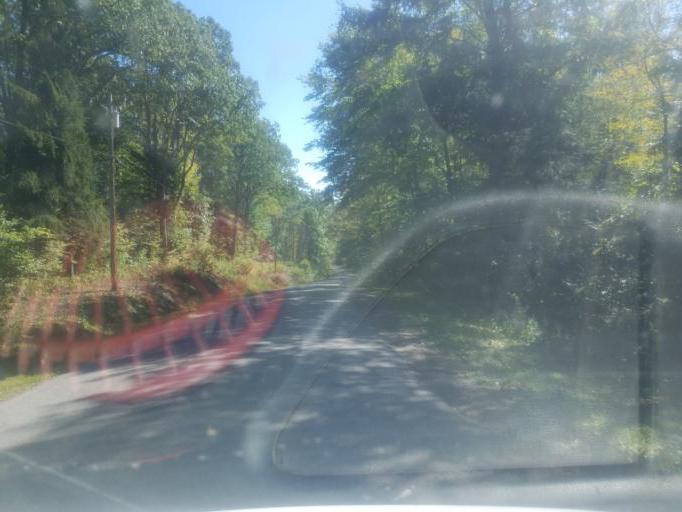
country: US
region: New York
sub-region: Allegany County
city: Cuba
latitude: 42.3092
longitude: -78.2031
